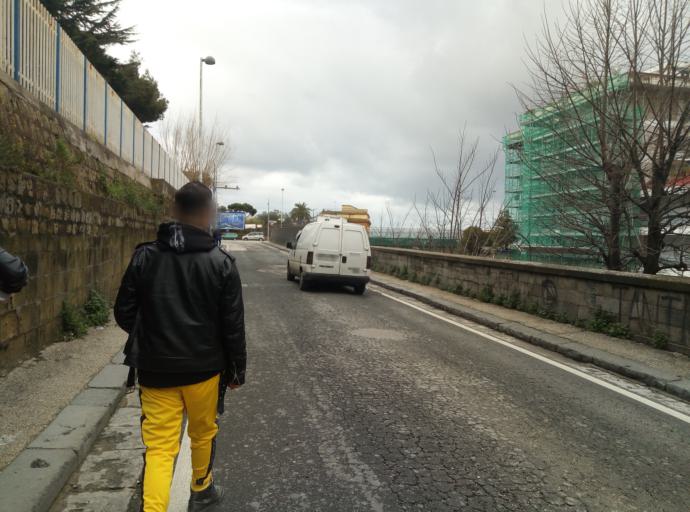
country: IT
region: Campania
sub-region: Provincia di Napoli
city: Napoli
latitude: 40.8594
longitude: 14.2255
